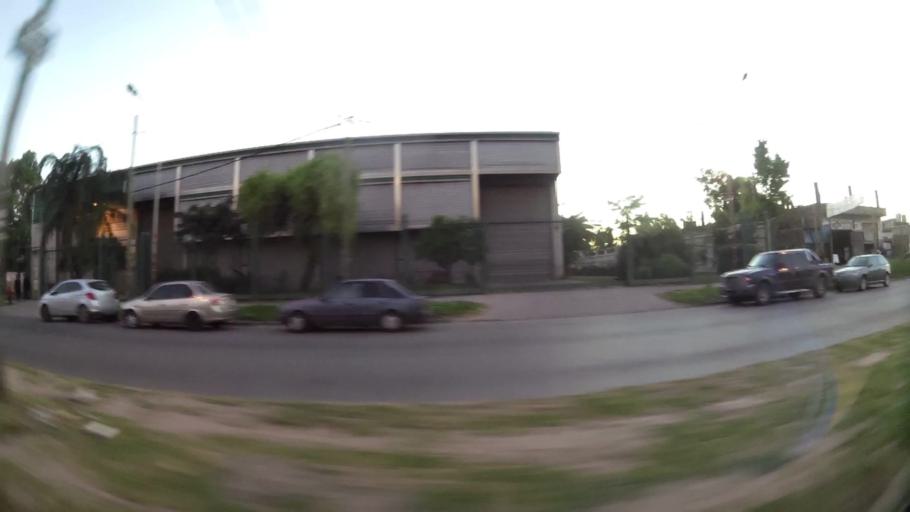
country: AR
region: Buenos Aires
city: San Justo
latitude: -34.7112
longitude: -58.6081
